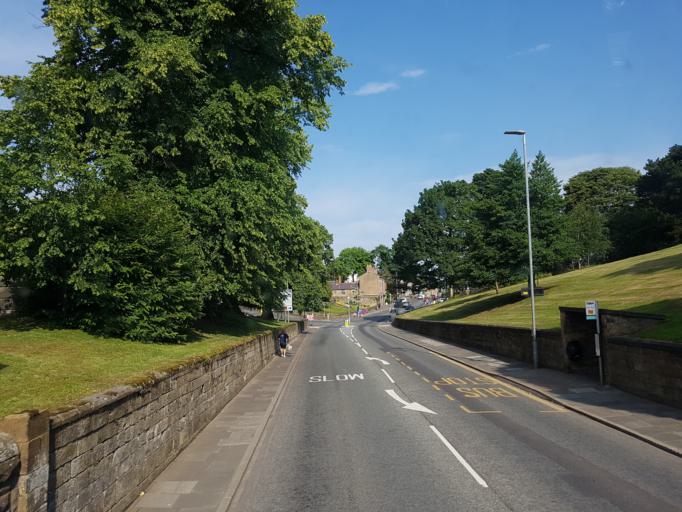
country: GB
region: England
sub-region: Northumberland
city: Alnwick
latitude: 55.4104
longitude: -1.6990
